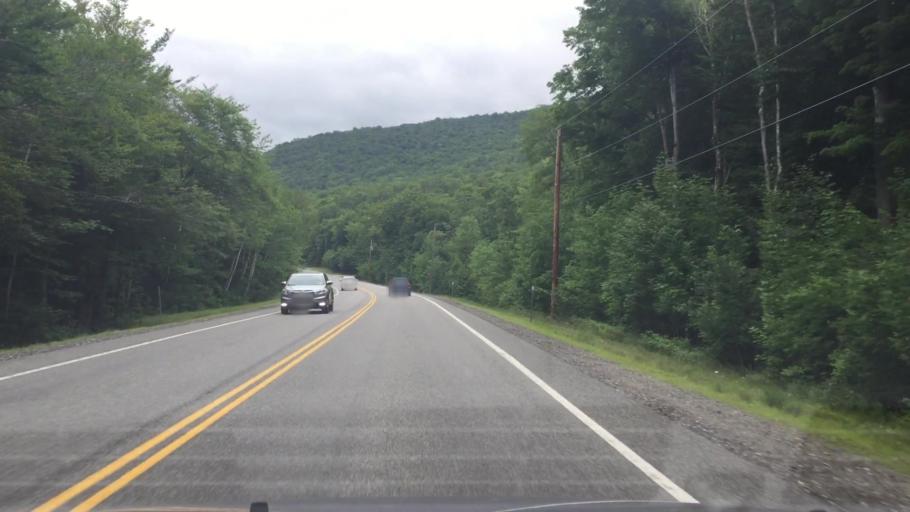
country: US
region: New Hampshire
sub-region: Carroll County
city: North Conway
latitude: 44.1320
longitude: -71.3602
